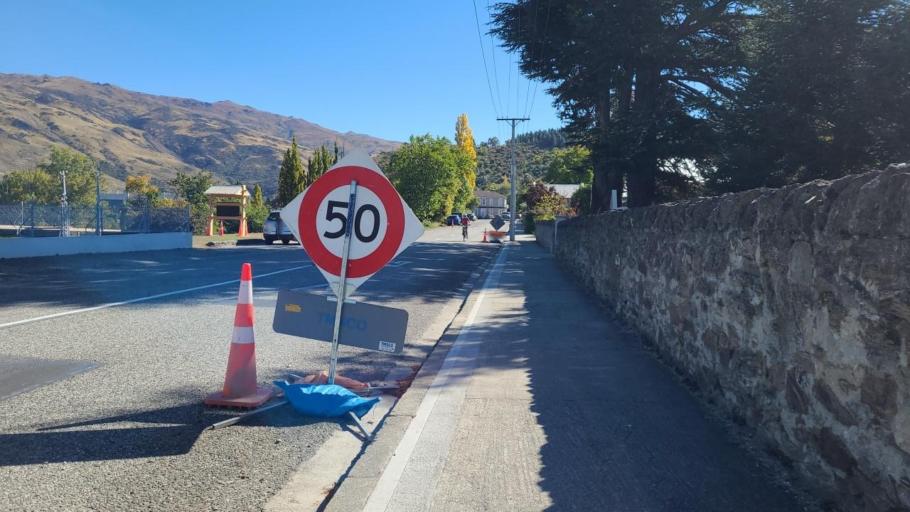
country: NZ
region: Otago
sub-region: Queenstown-Lakes District
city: Wanaka
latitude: -45.1890
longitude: 169.3171
